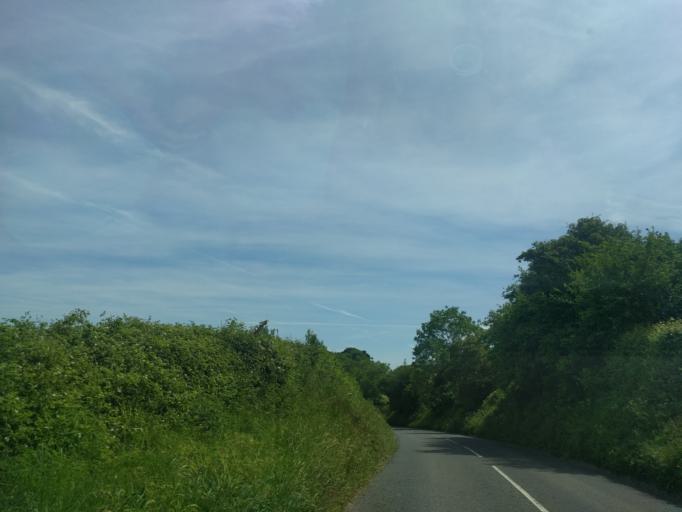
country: GB
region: England
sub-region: Wiltshire
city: Edington
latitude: 51.2802
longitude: -2.0806
